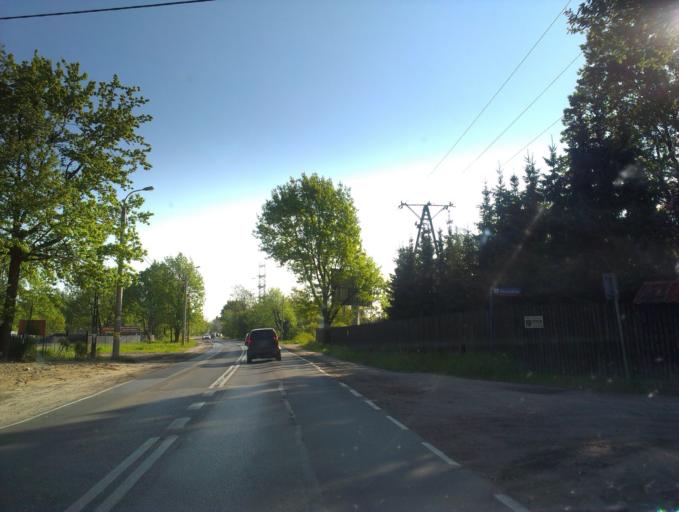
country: PL
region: Masovian Voivodeship
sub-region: Powiat piaseczynski
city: Konstancin-Jeziorna
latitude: 52.0872
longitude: 21.1019
